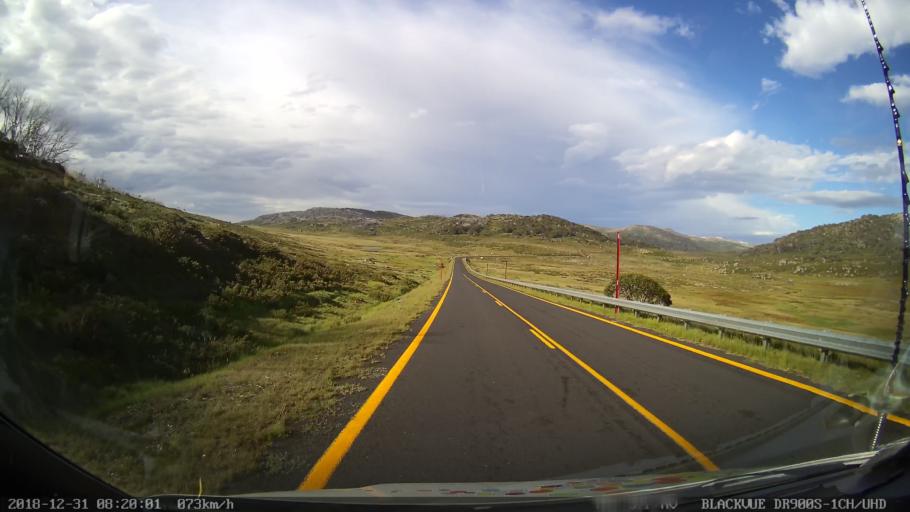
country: AU
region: New South Wales
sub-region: Snowy River
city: Jindabyne
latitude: -36.4228
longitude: 148.3793
